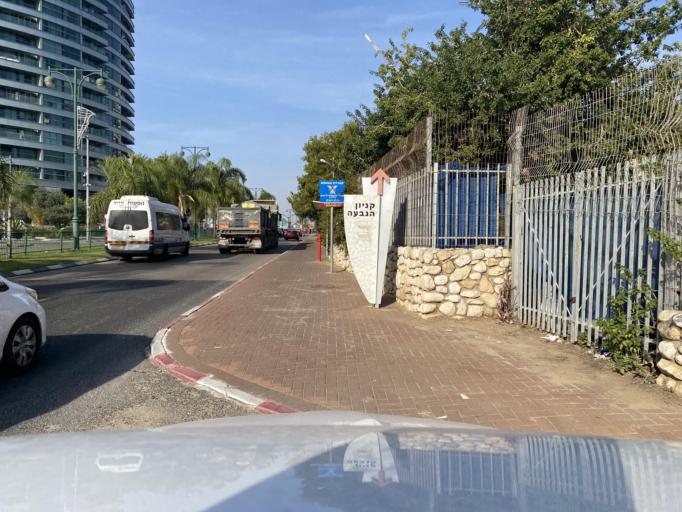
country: IL
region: Tel Aviv
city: Giv`at Shemu'el
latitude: 32.0682
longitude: 34.8500
